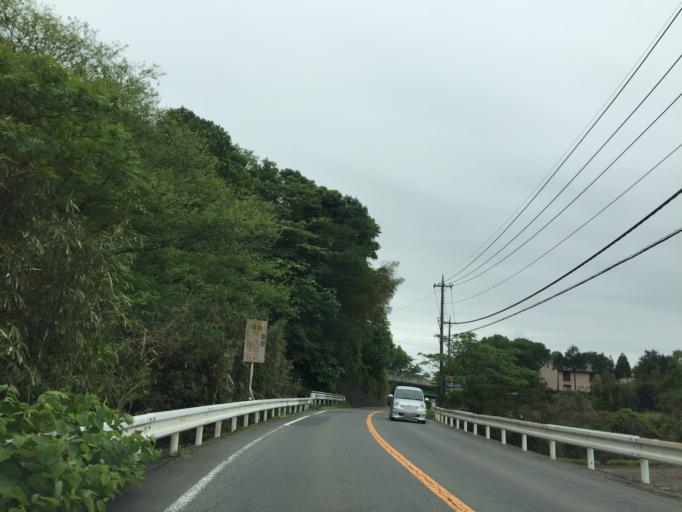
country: JP
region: Shizuoka
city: Mishima
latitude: 35.1775
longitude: 138.9202
